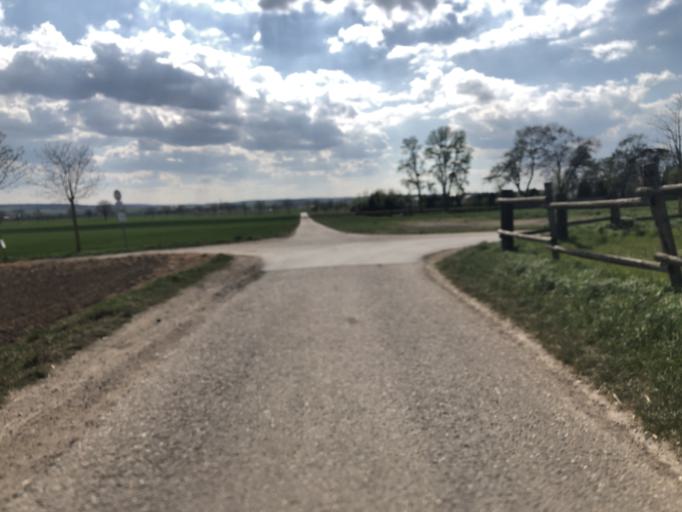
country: DE
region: North Rhine-Westphalia
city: Zulpich
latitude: 50.6835
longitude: 6.6494
